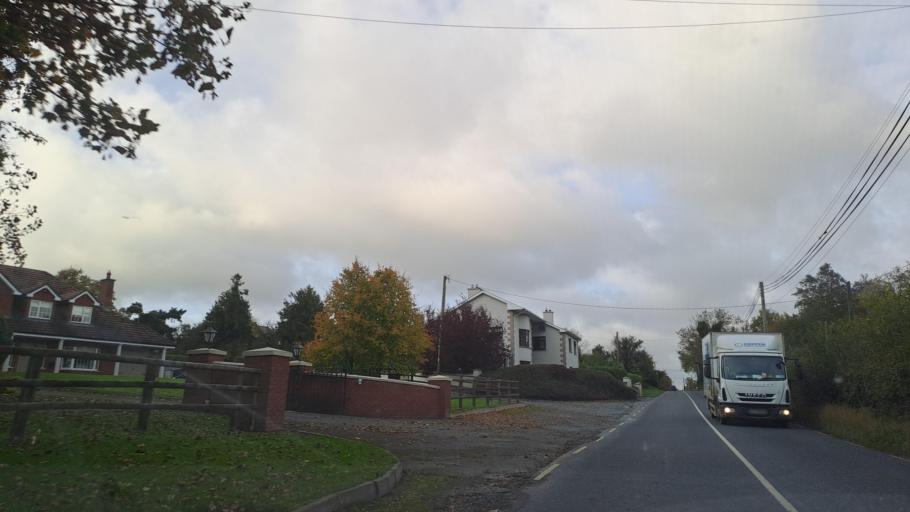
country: IE
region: Ulster
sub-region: An Cabhan
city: Kingscourt
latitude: 53.8911
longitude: -6.8025
